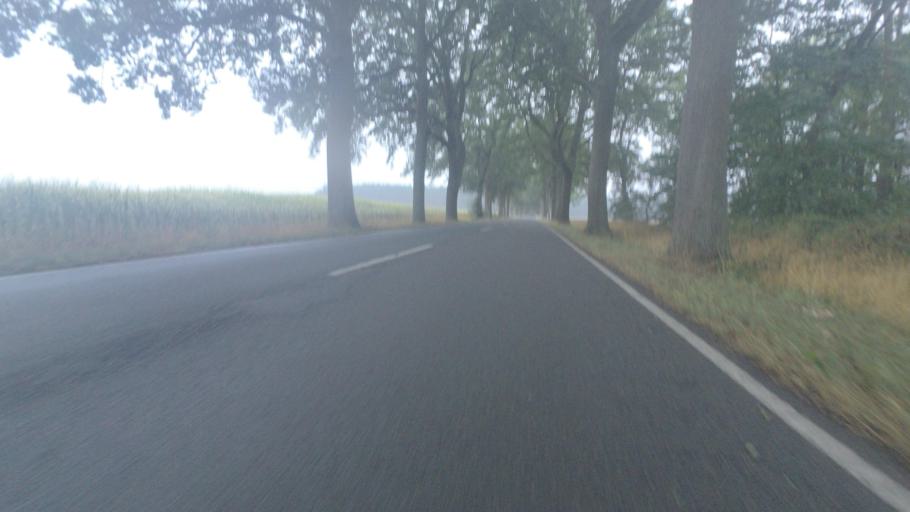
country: DE
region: Brandenburg
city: Heiligengrabe
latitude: 53.1086
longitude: 12.3701
